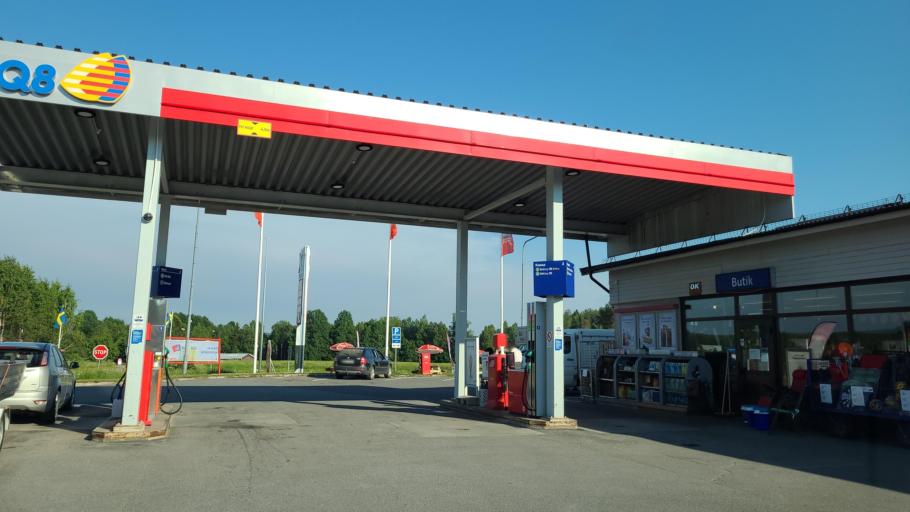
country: SE
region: Vaesterbotten
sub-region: Robertsfors Kommun
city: Robertsfors
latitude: 64.2725
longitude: 21.0473
